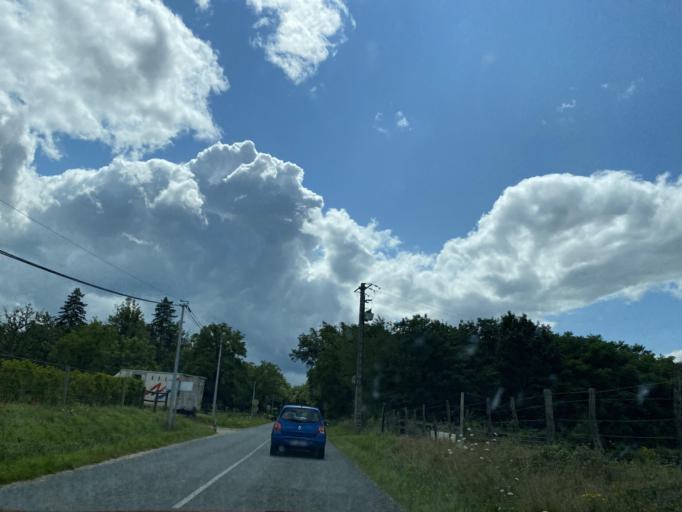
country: FR
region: Auvergne
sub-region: Departement du Puy-de-Dome
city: Peschadoires
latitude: 45.8239
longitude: 3.4863
